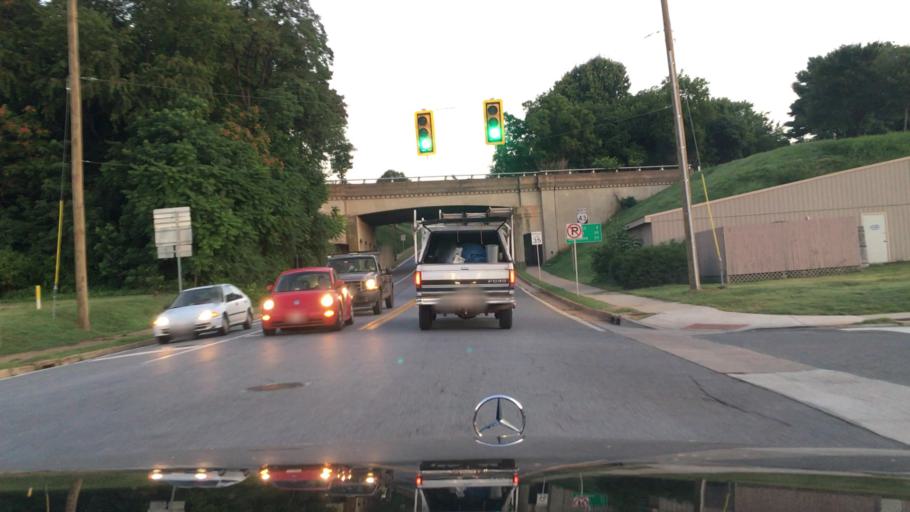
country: US
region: Virginia
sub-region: Campbell County
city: Altavista
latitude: 37.1082
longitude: -79.2922
